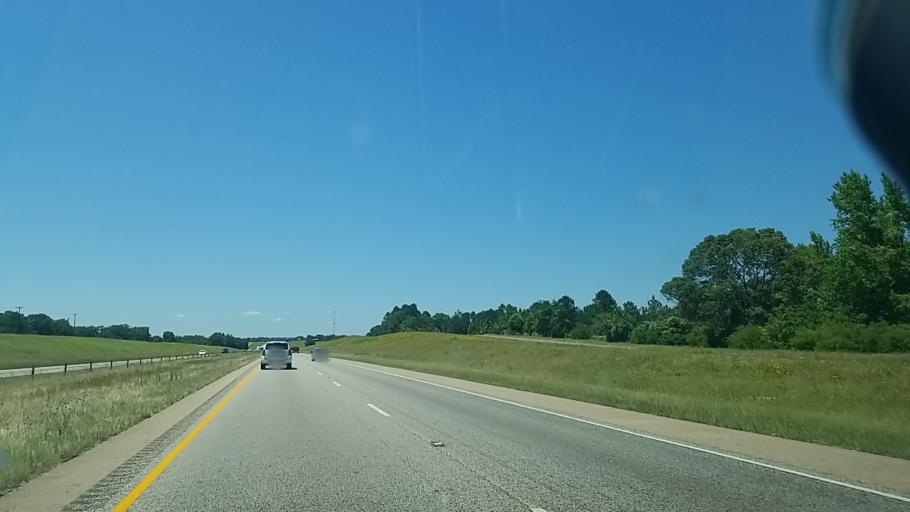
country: US
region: Texas
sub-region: Leon County
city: Buffalo
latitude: 31.4035
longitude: -96.0371
